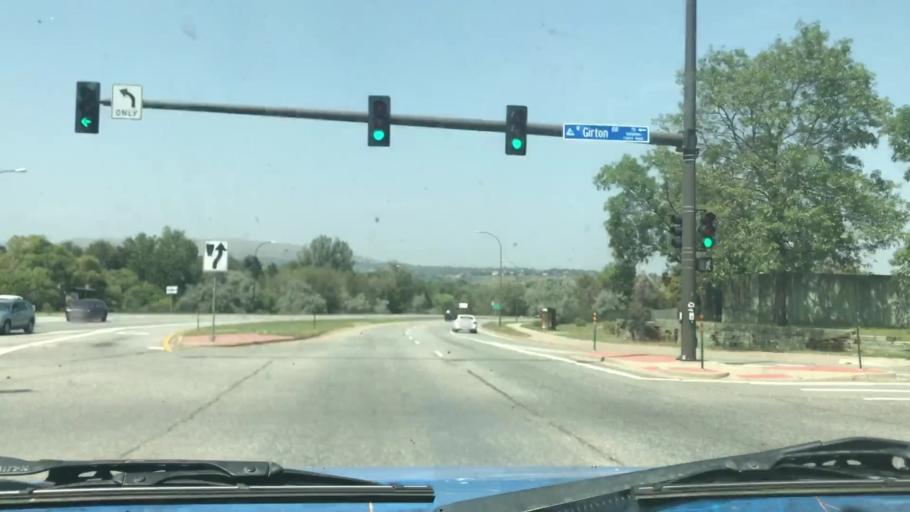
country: US
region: Colorado
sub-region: Jefferson County
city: Lakewood
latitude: 39.6561
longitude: -105.1107
